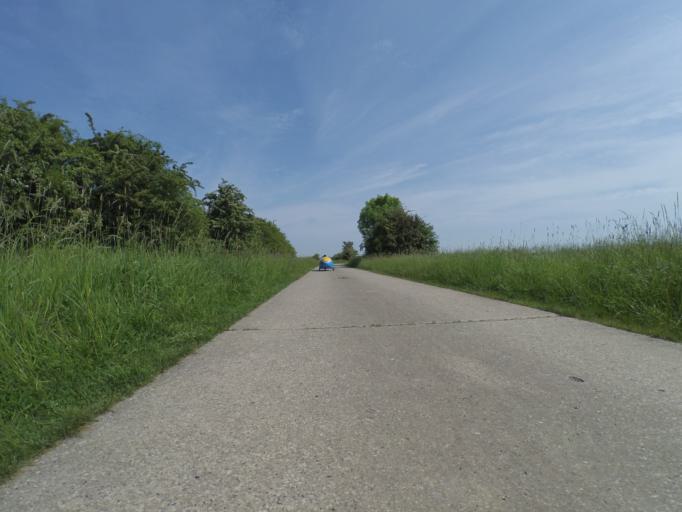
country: DE
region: Lower Saxony
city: Sehnde
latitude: 52.2977
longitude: 9.9652
